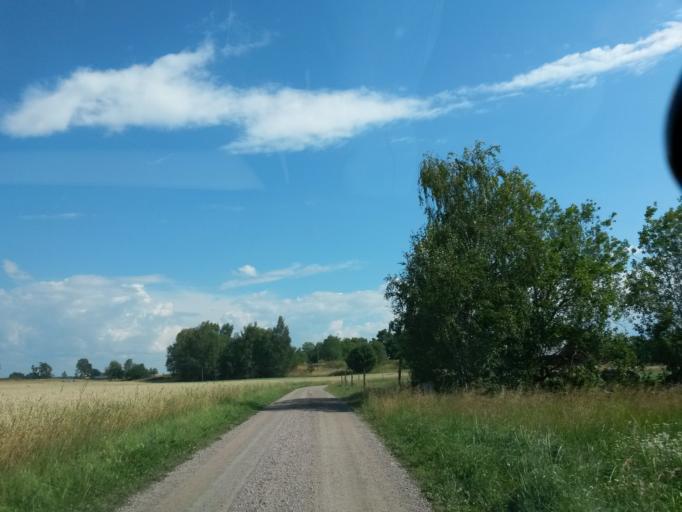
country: SE
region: Vaestra Goetaland
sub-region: Grastorps Kommun
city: Graestorp
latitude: 58.3455
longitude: 12.7659
